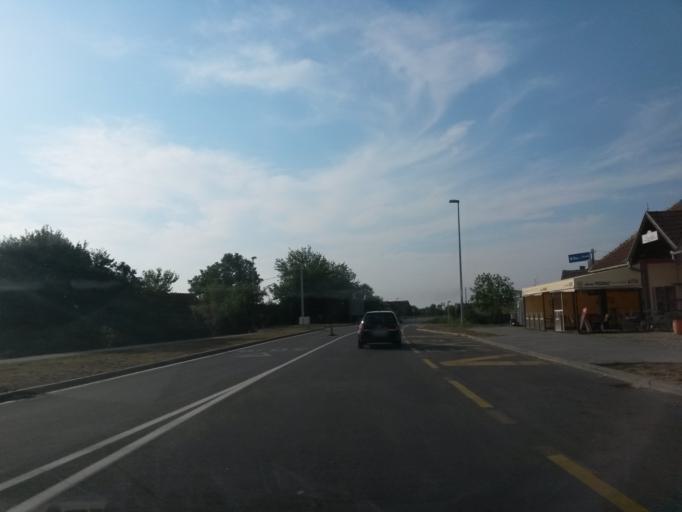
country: HR
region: Brodsko-Posavska
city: Vrpolje
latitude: 45.2106
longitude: 18.4049
